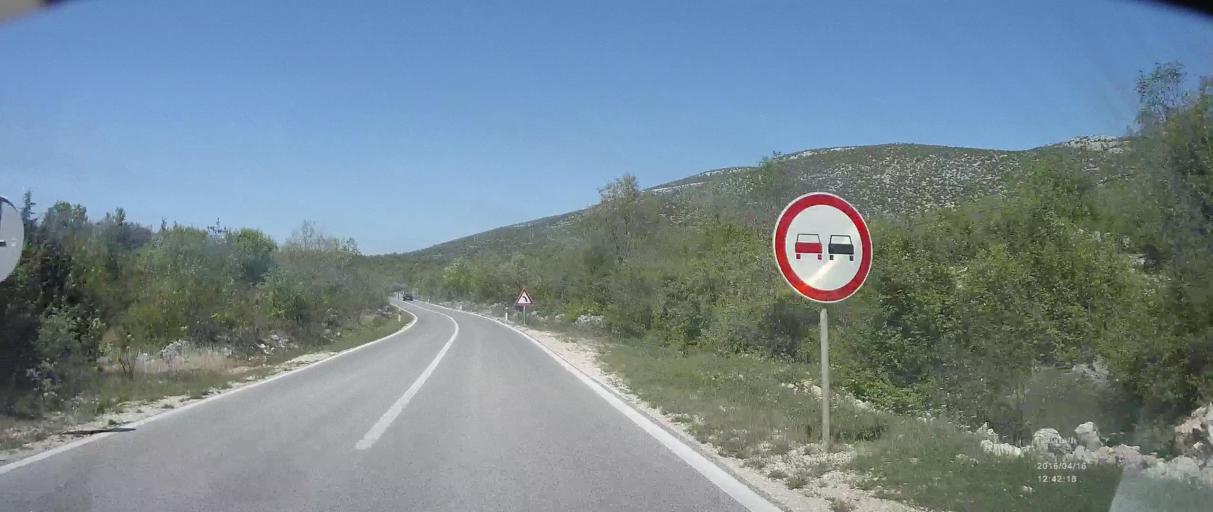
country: HR
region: Sibensko-Kniniska
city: Rogoznica
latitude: 43.6282
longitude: 16.0912
